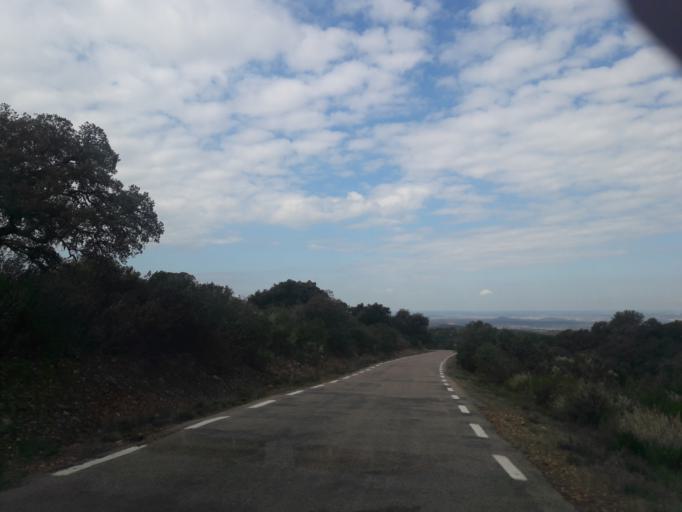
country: ES
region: Castille and Leon
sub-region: Provincia de Salamanca
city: Serradilla del Arroyo
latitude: 40.5405
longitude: -6.3919
